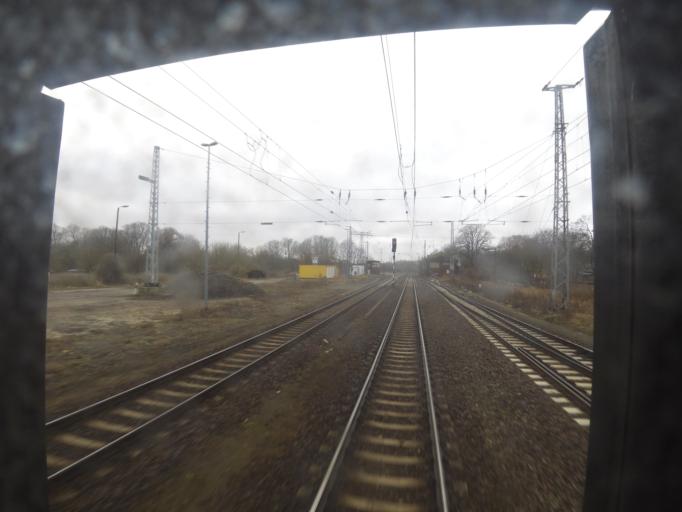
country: DE
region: Brandenburg
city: Zossen
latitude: 52.2152
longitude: 13.4390
